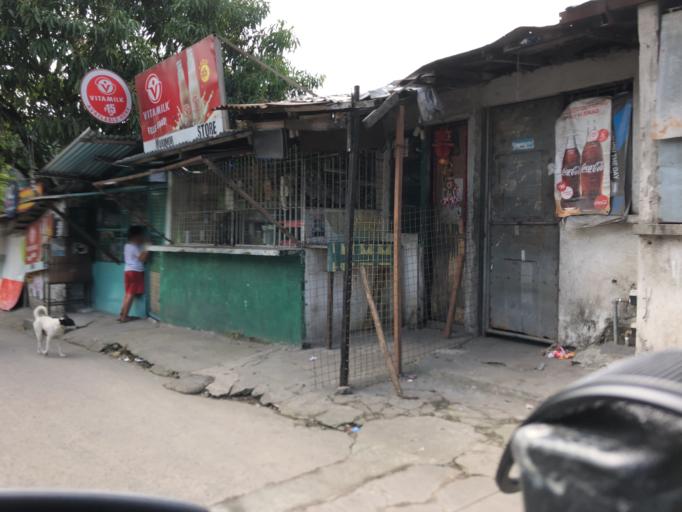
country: PH
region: Central Luzon
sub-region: Province of Bulacan
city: San Jose del Monte
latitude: 14.7597
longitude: 121.0511
